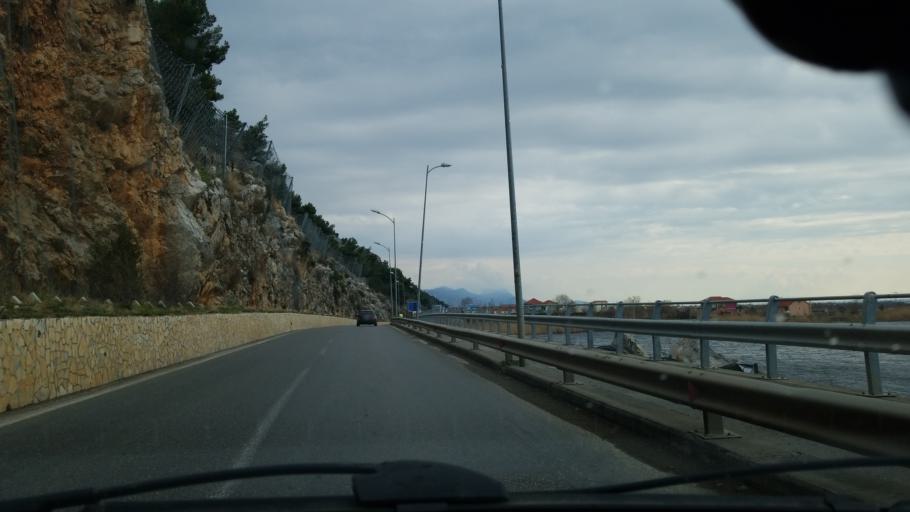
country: AL
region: Lezhe
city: Shengjin
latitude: 41.8029
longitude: 19.6147
